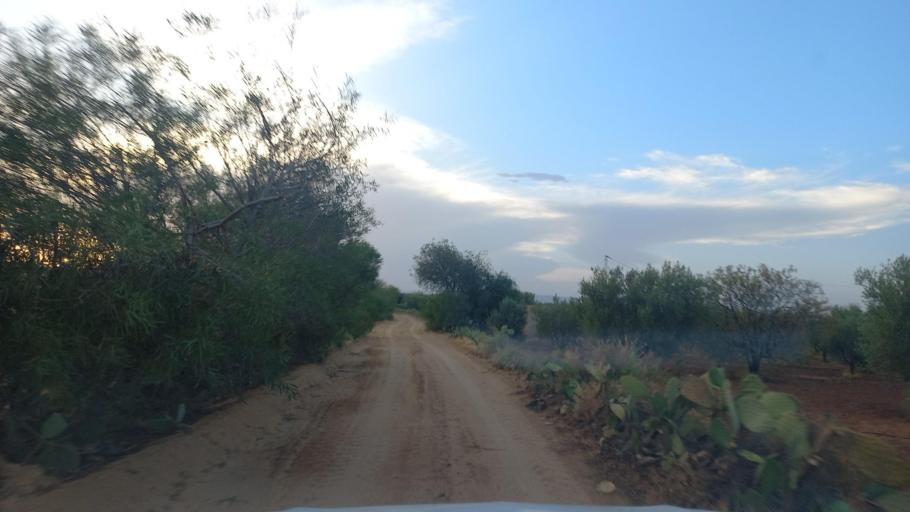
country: TN
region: Al Qasrayn
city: Kasserine
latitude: 35.2117
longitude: 9.0484
